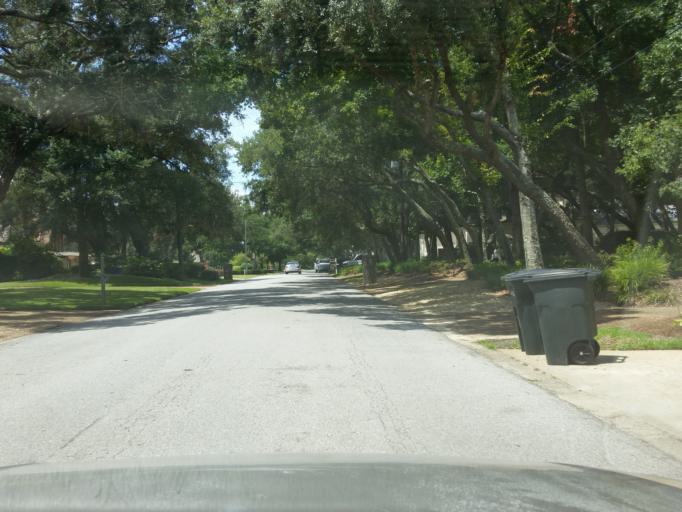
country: US
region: Florida
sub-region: Santa Rosa County
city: Gulf Breeze
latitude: 30.3668
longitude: -87.1649
